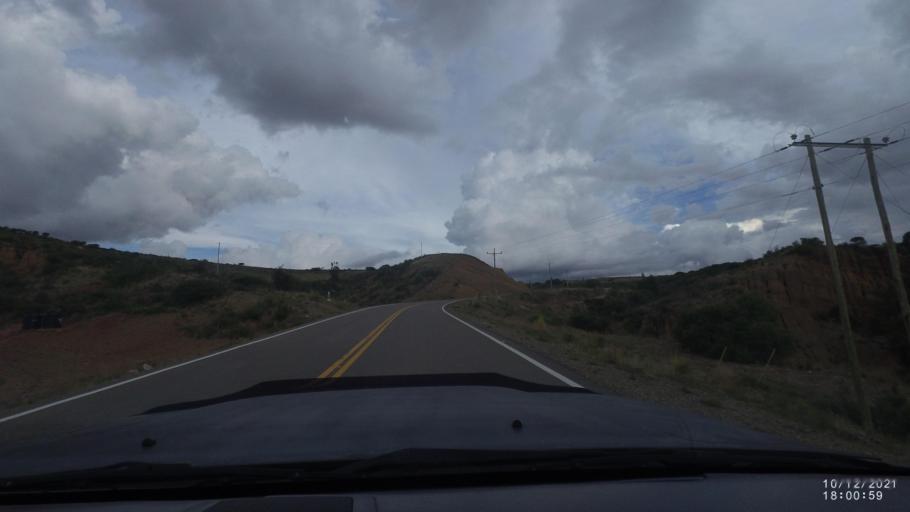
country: BO
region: Cochabamba
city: Cliza
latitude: -17.7462
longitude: -65.9203
